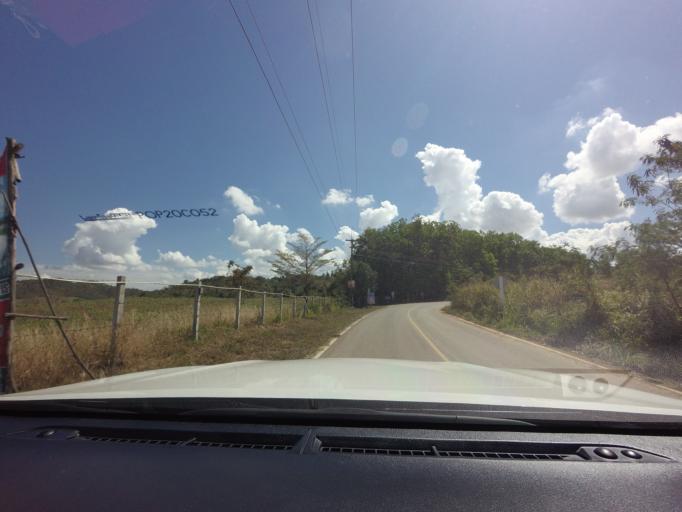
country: TH
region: Nakhon Ratchasima
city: Wang Nam Khiao
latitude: 14.4351
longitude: 101.7097
